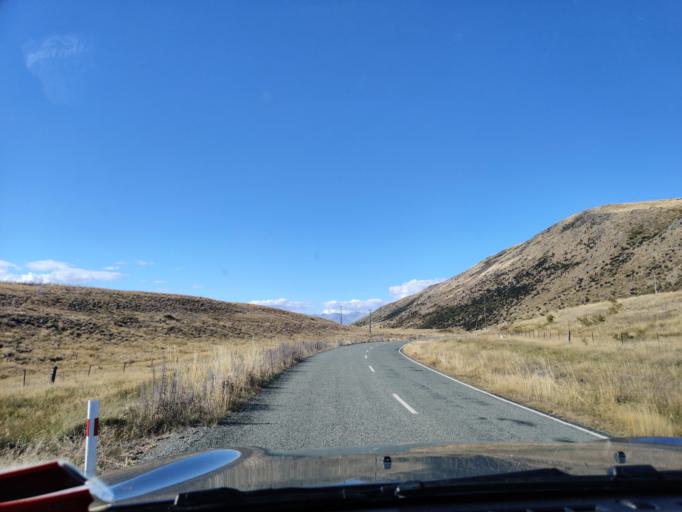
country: NZ
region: Canterbury
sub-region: Timaru District
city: Pleasant Point
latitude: -43.9899
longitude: 170.4507
